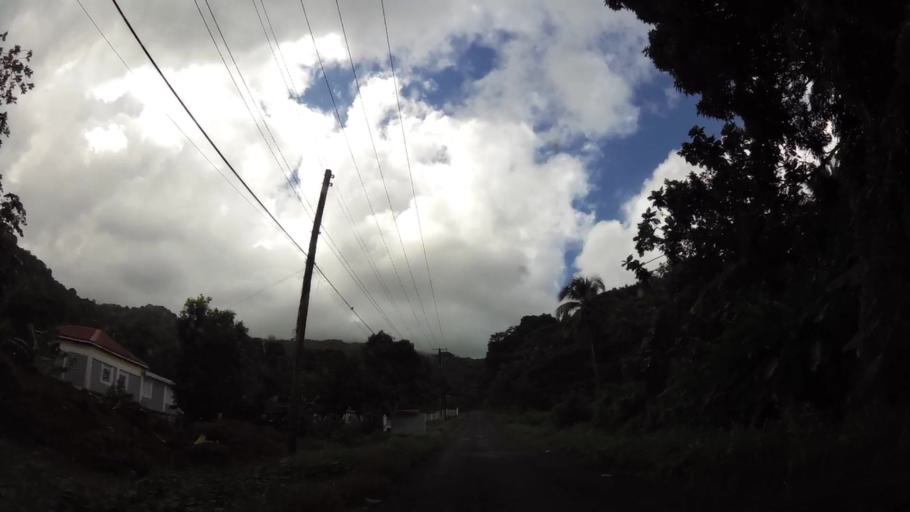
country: DM
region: Saint David
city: Castle Bruce
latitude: 15.4026
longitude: -61.3058
